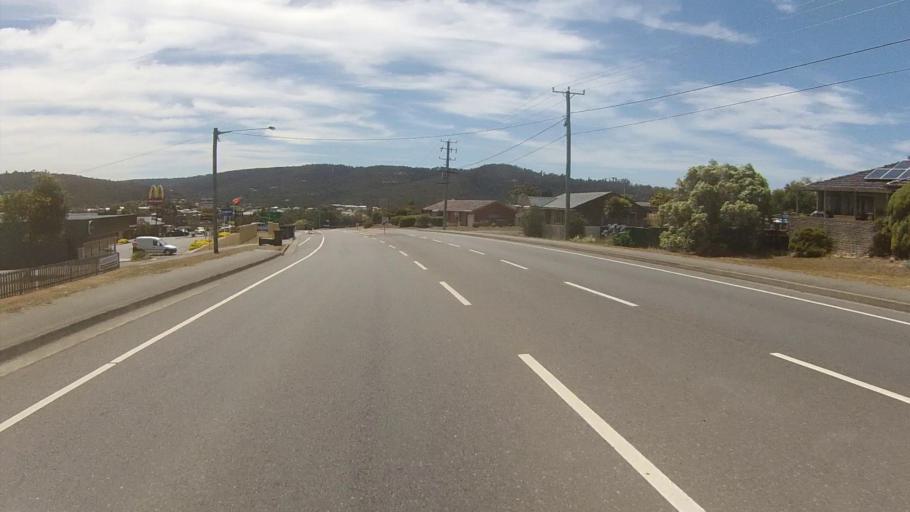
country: AU
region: Tasmania
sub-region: Kingborough
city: Kingston
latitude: -42.9774
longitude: 147.3029
